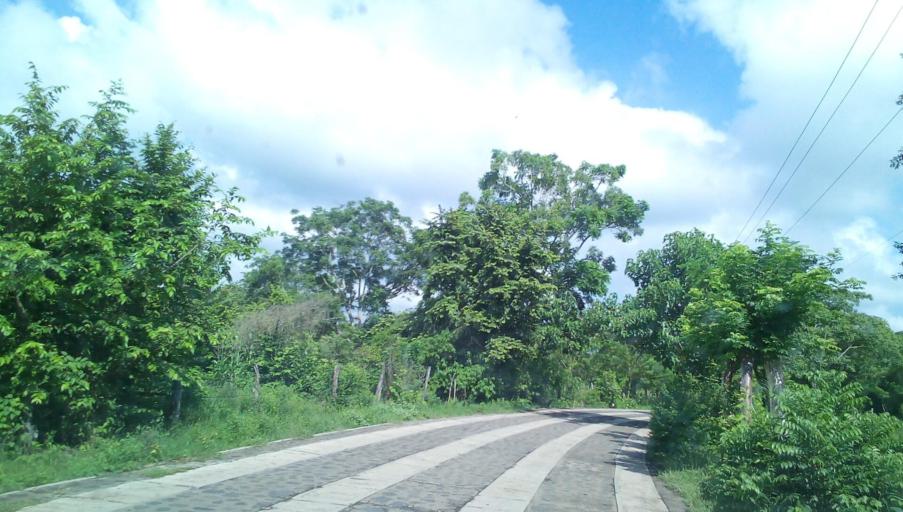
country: MX
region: Veracruz
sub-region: Citlaltepetl
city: Las Sabinas
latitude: 21.3481
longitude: -97.8938
